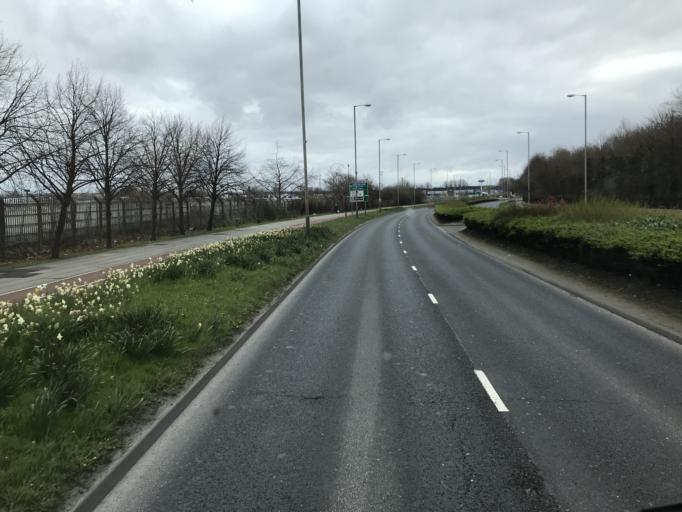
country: GB
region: England
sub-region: Knowsley
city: Huyton
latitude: 53.3499
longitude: -2.8713
